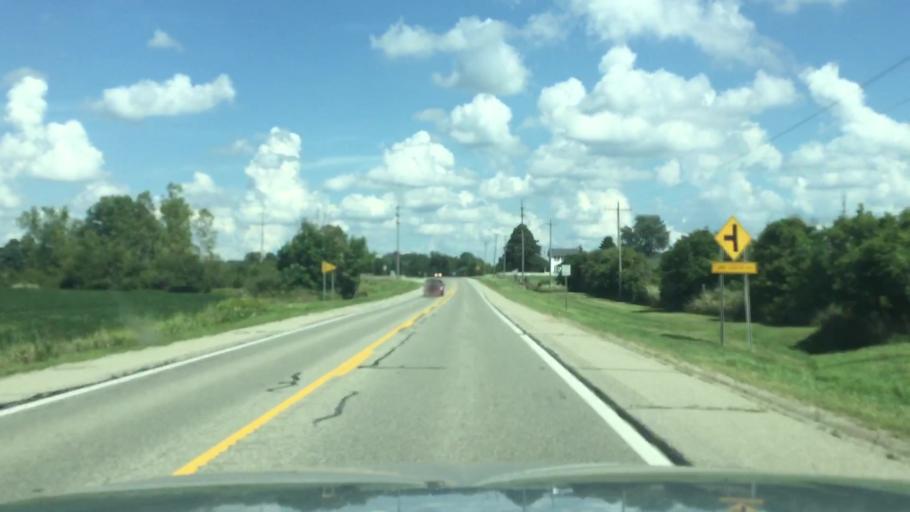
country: US
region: Michigan
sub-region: Lenawee County
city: Clinton
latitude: 42.0822
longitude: -83.9506
